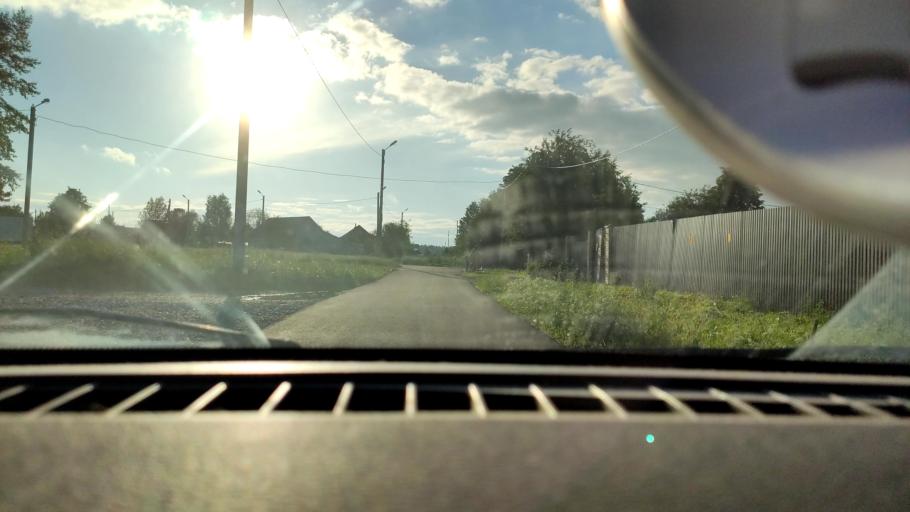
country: RU
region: Perm
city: Novyye Lyady
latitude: 58.0564
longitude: 56.6025
